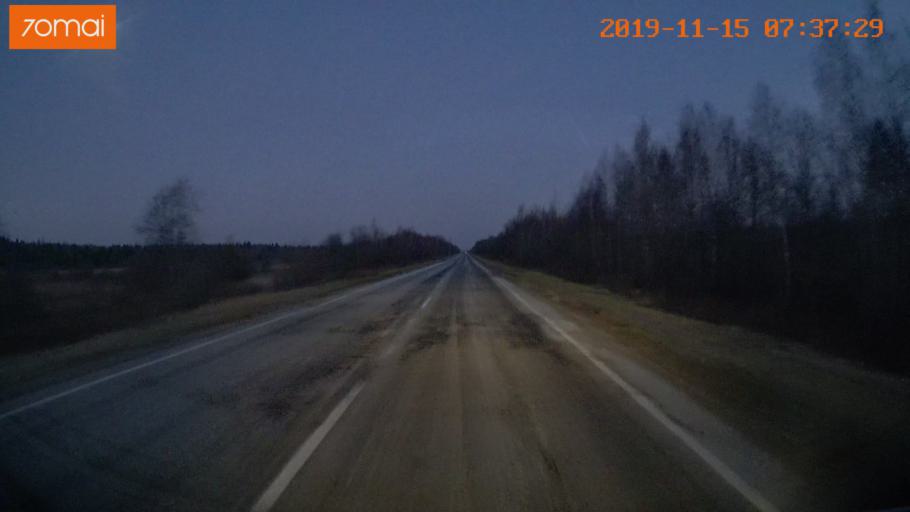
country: RU
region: Vologda
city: Sheksna
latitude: 58.7469
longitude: 38.4213
